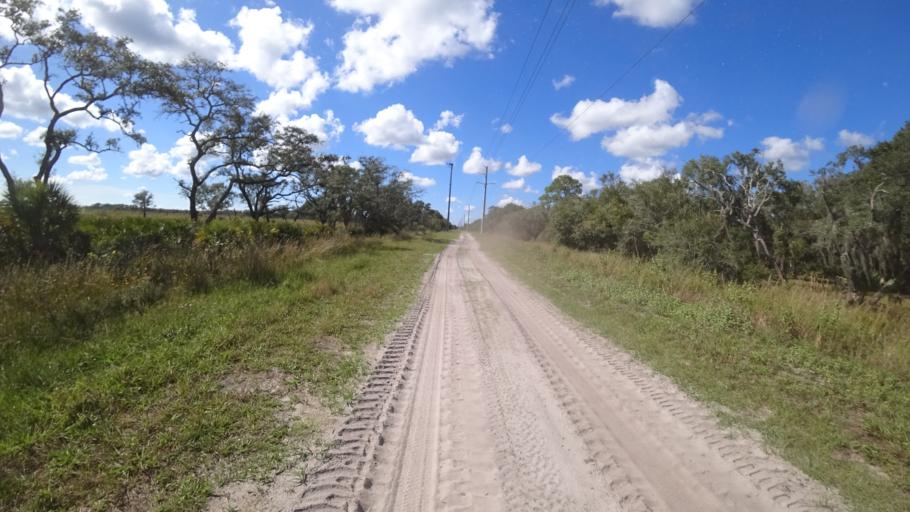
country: US
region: Florida
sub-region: Sarasota County
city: Lake Sarasota
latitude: 27.2448
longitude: -82.2725
